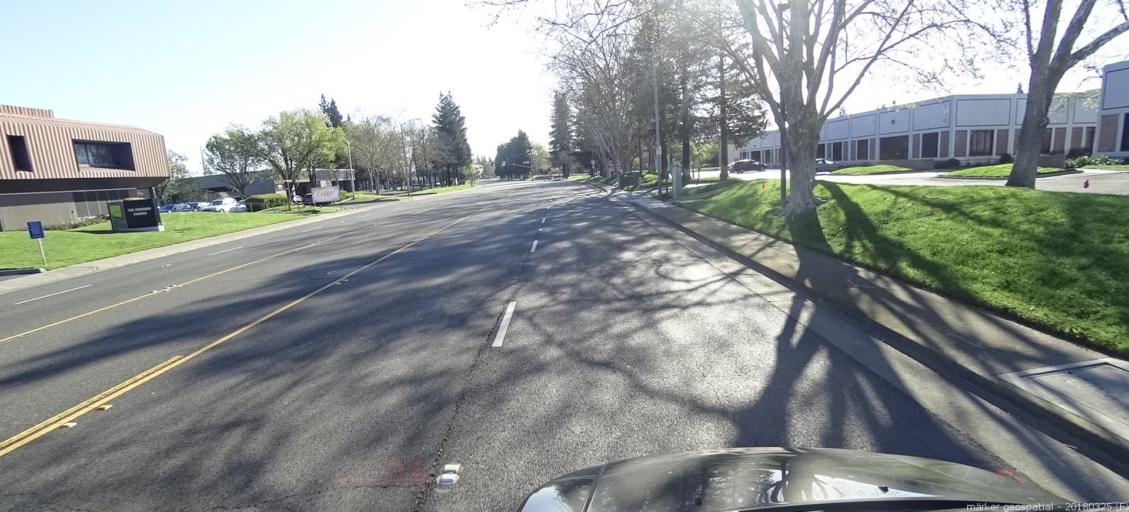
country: US
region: California
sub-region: Sacramento County
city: Rio Linda
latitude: 38.6467
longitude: -121.4902
